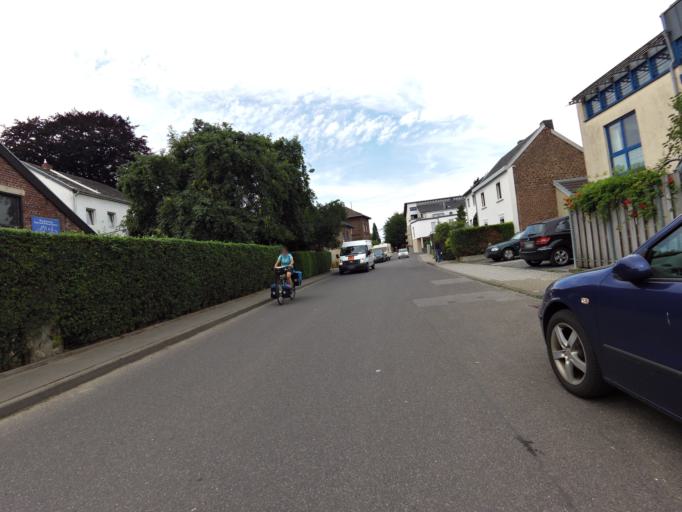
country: NL
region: Limburg
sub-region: Gemeente Vaals
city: Vaals
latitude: 50.8144
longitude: 6.0426
